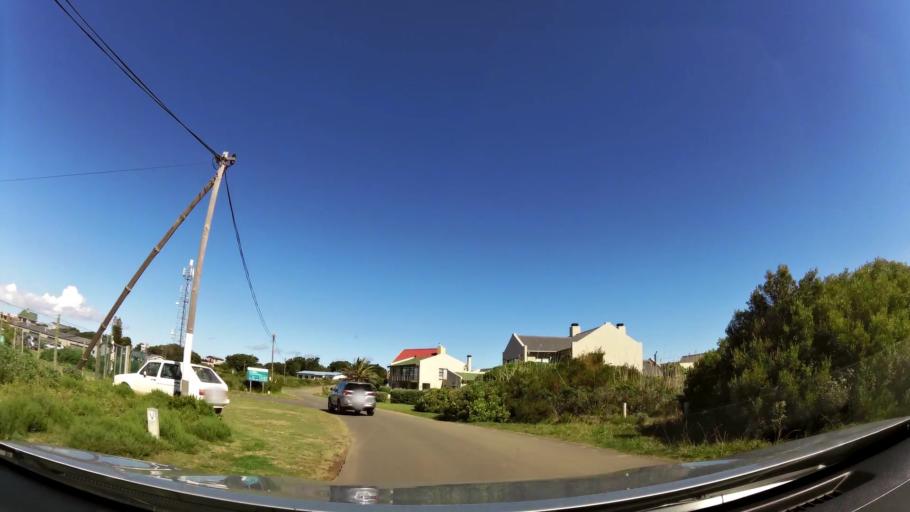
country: ZA
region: Western Cape
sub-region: Overberg District Municipality
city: Grabouw
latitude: -34.3708
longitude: 18.8920
